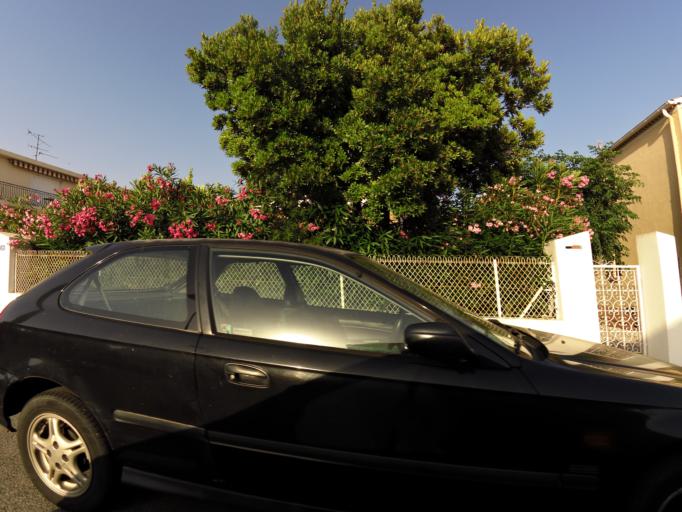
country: FR
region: Provence-Alpes-Cote d'Azur
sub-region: Departement du Var
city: Hyeres
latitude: 43.1175
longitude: 6.1388
